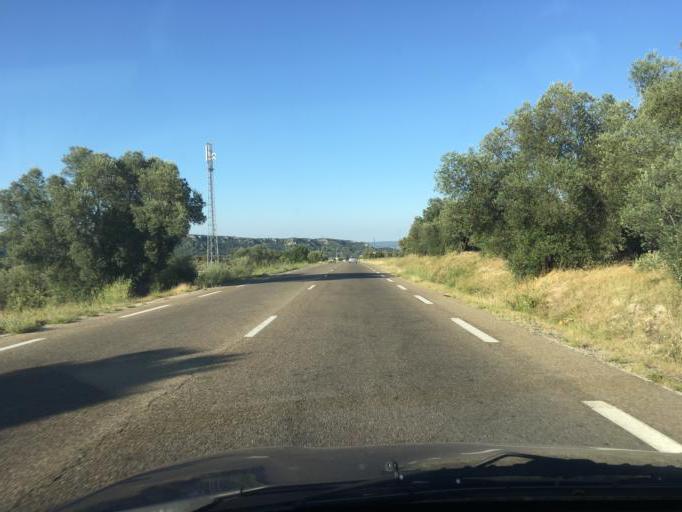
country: FR
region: Languedoc-Roussillon
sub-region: Departement du Gard
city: Ledenon
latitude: 43.9163
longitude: 4.5304
